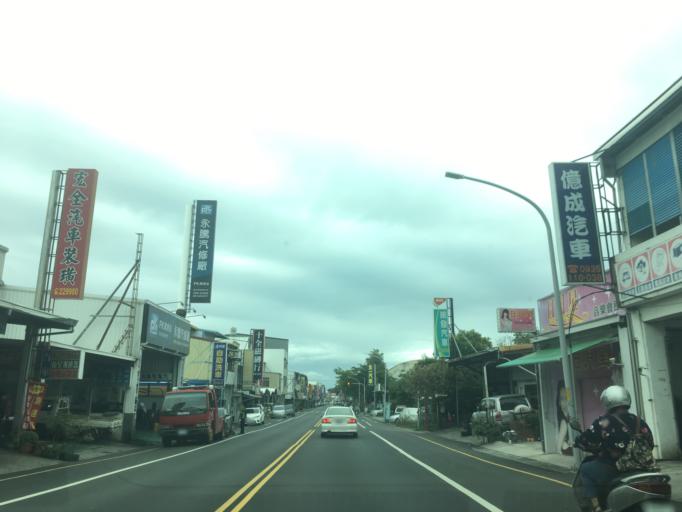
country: TW
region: Taiwan
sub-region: Taitung
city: Taitung
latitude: 22.7656
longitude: 121.1339
